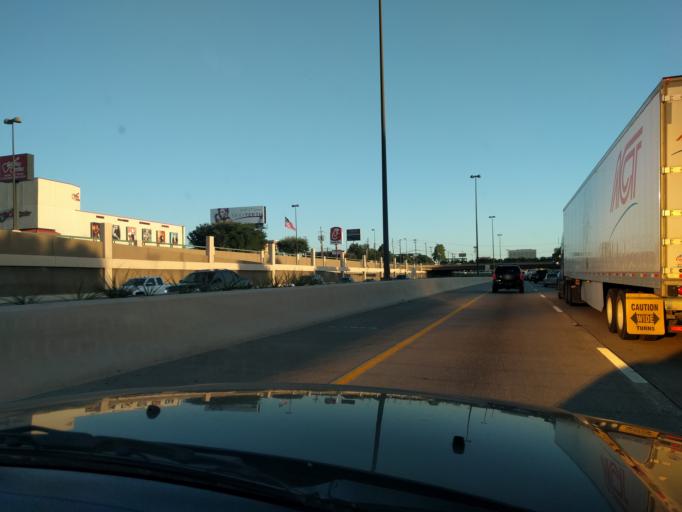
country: US
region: Texas
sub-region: Dallas County
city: University Park
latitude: 32.8594
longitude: -96.7704
